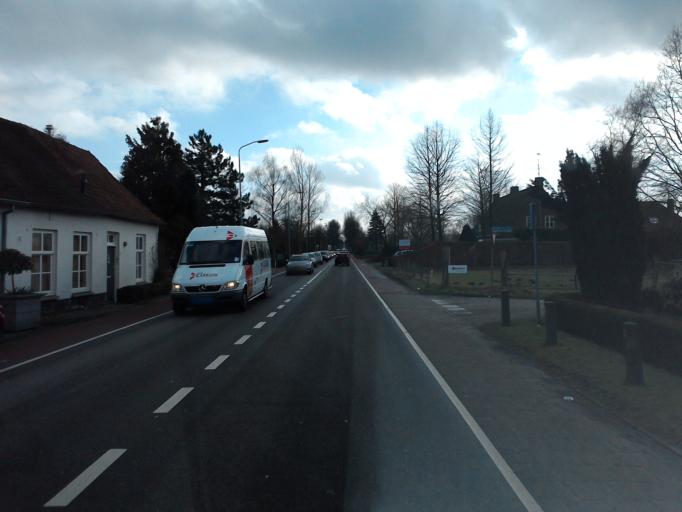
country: NL
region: North Brabant
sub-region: Gemeente Boxtel
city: Boxtel
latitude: 51.5807
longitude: 5.3355
